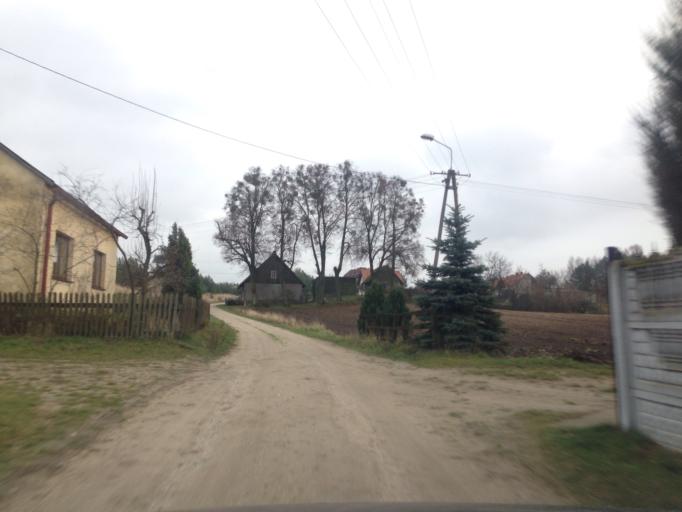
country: PL
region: Kujawsko-Pomorskie
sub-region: Powiat brodnicki
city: Gorzno
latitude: 53.2100
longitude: 19.6690
